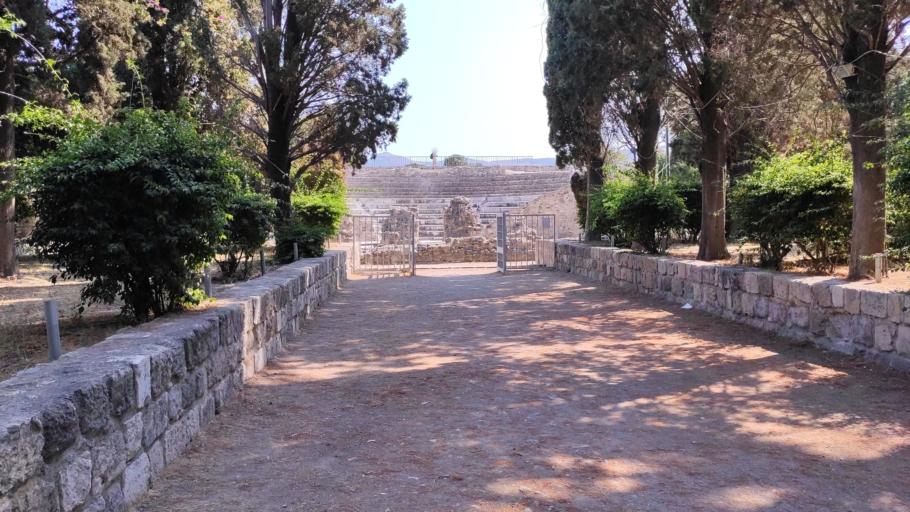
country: GR
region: South Aegean
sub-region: Nomos Dodekanisou
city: Kos
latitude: 36.8900
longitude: 27.2848
